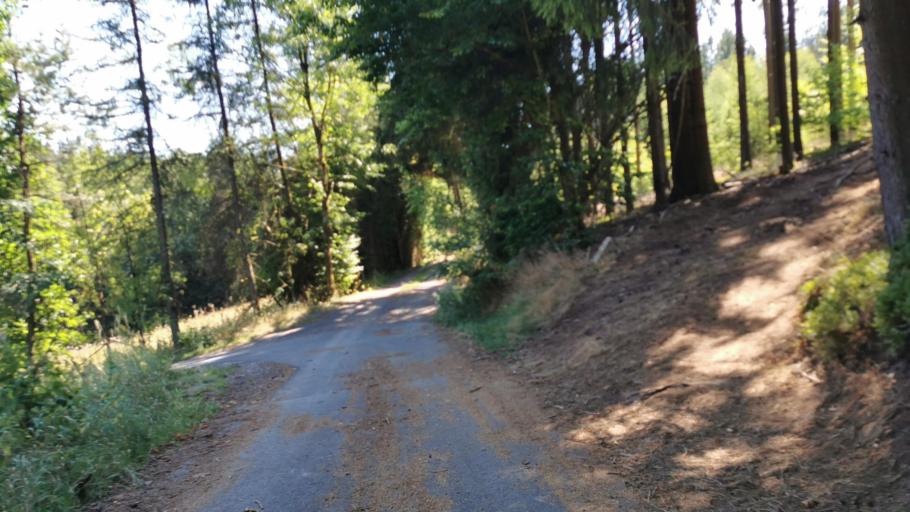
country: DE
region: Bavaria
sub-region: Upper Franconia
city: Tettau
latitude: 50.4168
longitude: 11.2928
